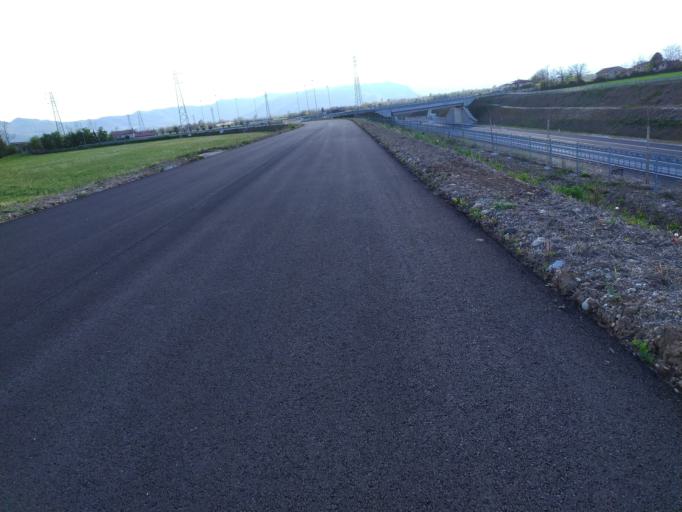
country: IT
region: Veneto
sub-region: Provincia di Vicenza
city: Villaverla
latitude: 45.6609
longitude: 11.4883
